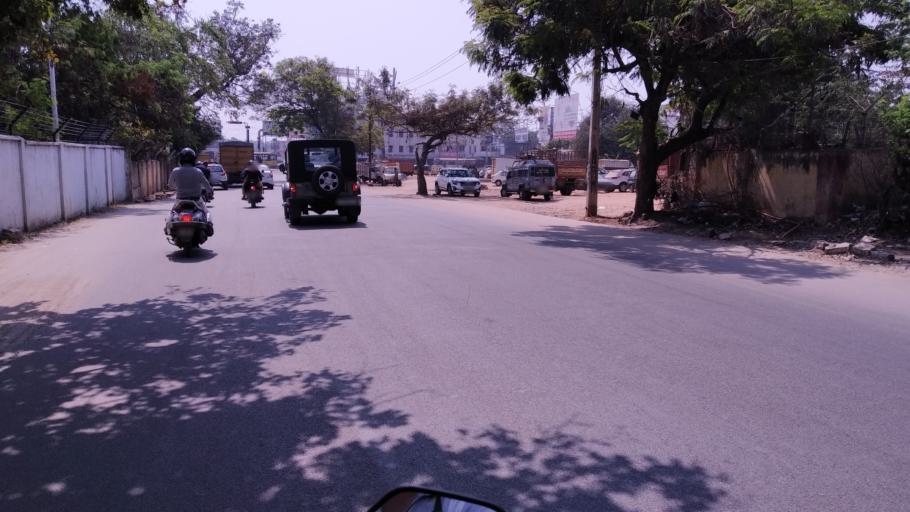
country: IN
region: Telangana
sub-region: Hyderabad
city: Malkajgiri
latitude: 17.4581
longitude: 78.4849
